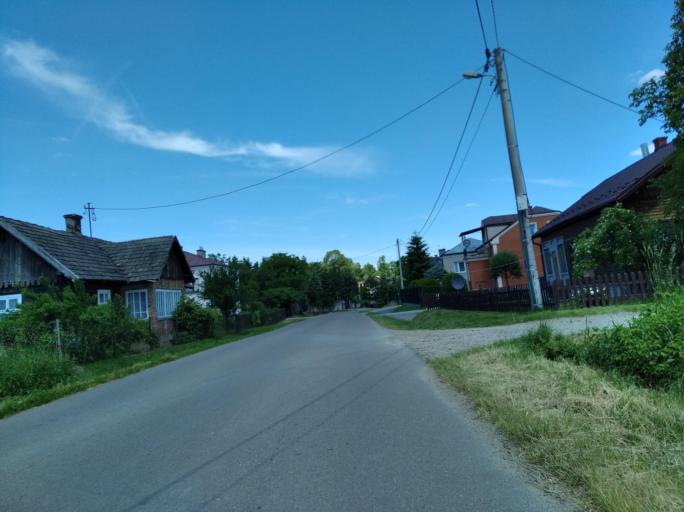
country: PL
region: Subcarpathian Voivodeship
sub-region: Powiat jasielski
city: Osiek Jasielski
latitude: 49.6649
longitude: 21.5429
